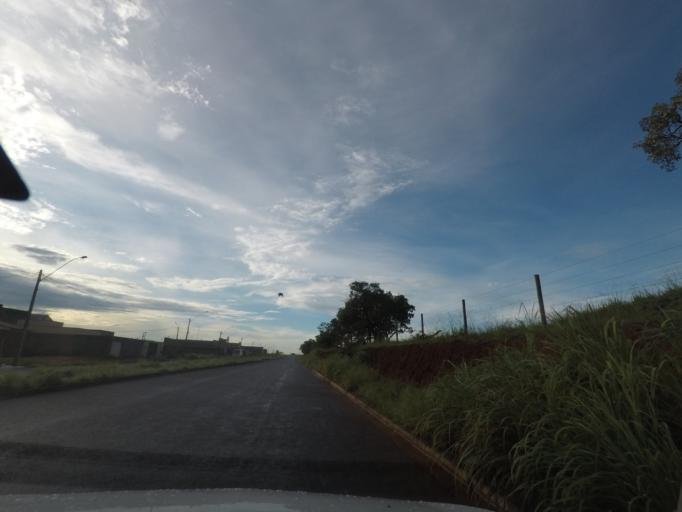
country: BR
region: Goias
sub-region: Trindade
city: Trindade
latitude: -16.7517
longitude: -49.3833
